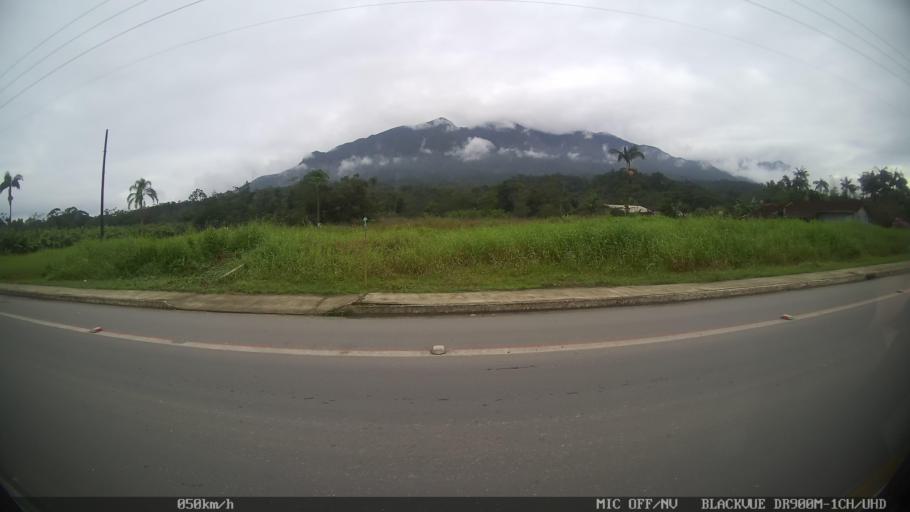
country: BR
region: Santa Catarina
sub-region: Joinville
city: Joinville
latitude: -26.0568
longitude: -48.8570
